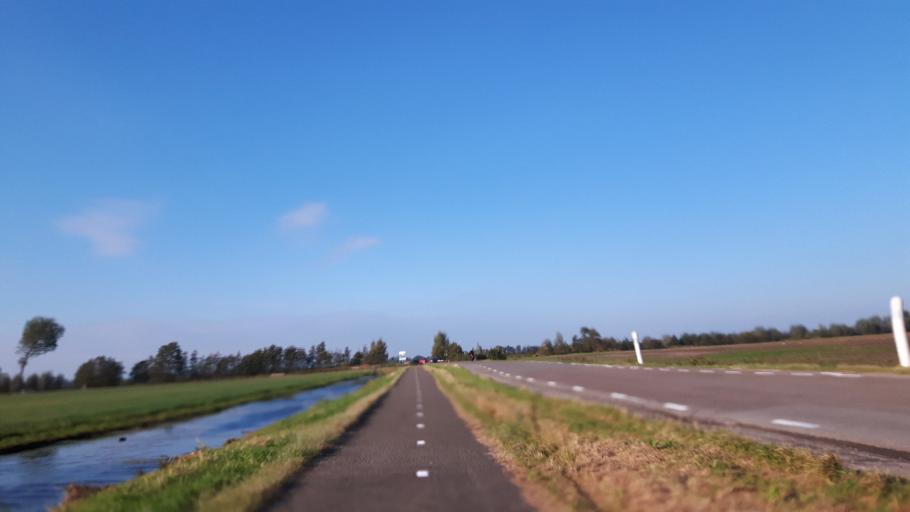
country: NL
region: Utrecht
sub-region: Gemeente Oudewater
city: Oudewater
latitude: 52.0036
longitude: 4.8979
